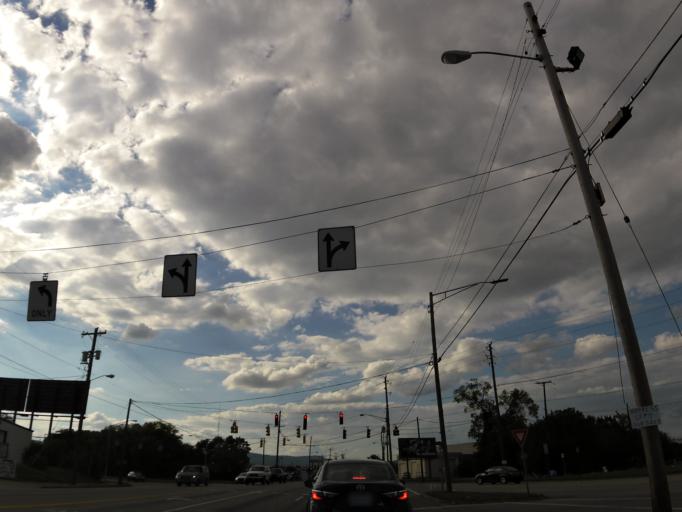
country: US
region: Tennessee
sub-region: Hamilton County
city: Chattanooga
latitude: 35.0241
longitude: -85.2976
